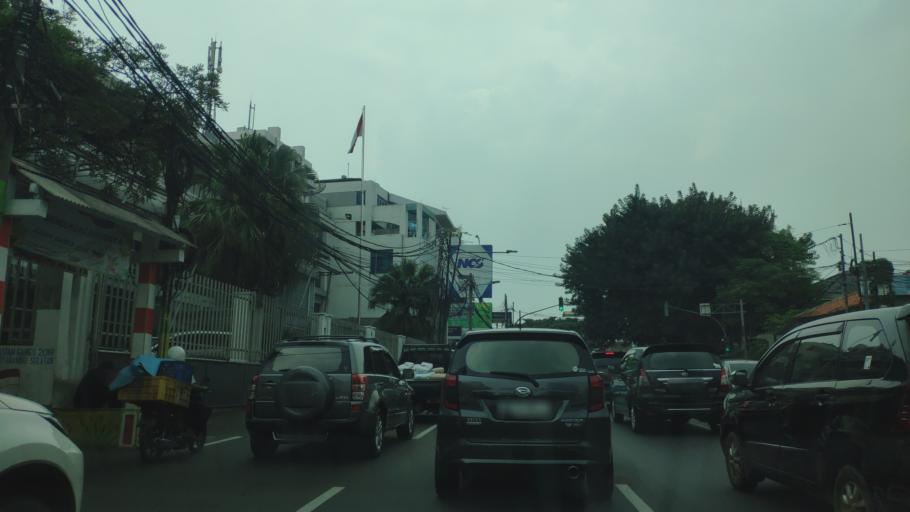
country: ID
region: Jakarta Raya
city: Jakarta
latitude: -6.1893
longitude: 106.8005
